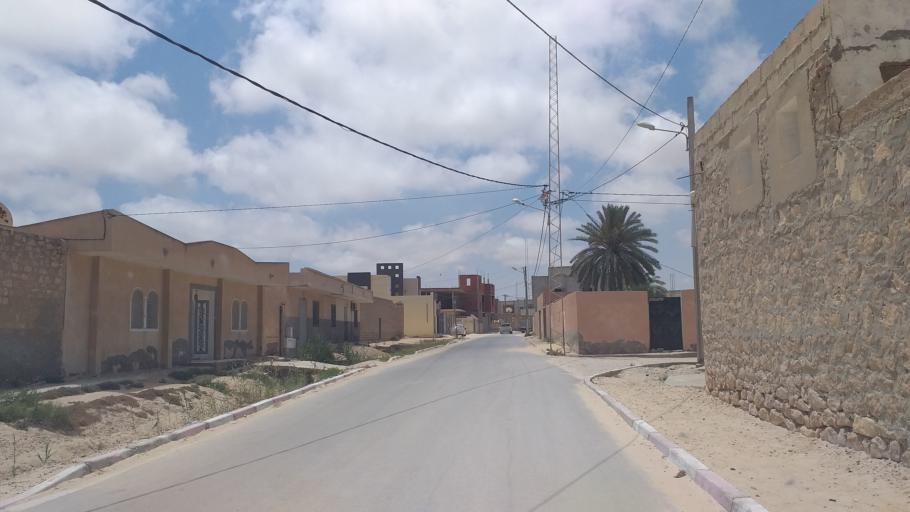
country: TN
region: Qabis
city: Gabes
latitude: 33.9367
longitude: 10.0627
